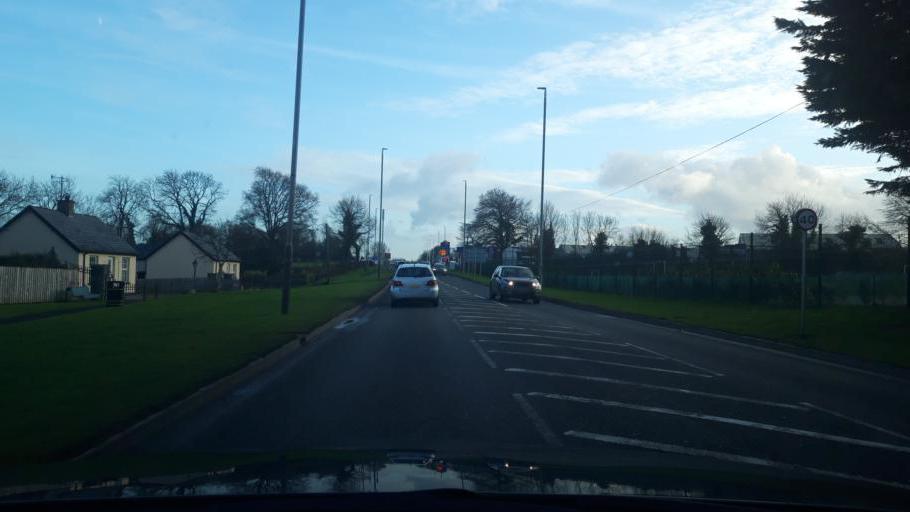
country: GB
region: Northern Ireland
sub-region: Dungannon District
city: Dungannon
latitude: 54.4881
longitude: -6.7465
